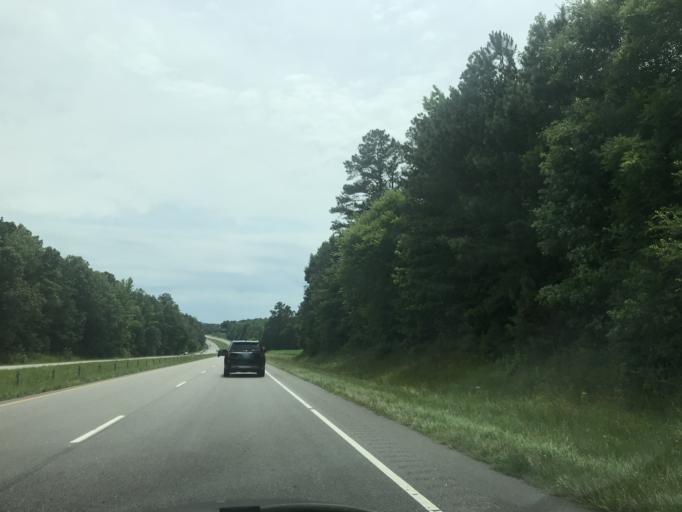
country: US
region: North Carolina
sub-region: Vance County
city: South Henderson
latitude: 36.2569
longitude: -78.4262
